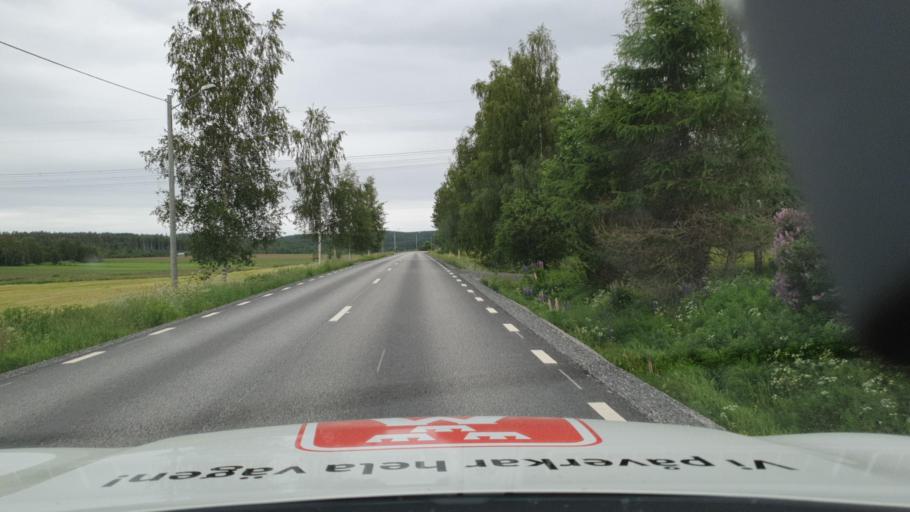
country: SE
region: Vaesterbotten
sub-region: Vannas Kommun
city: Vaennaes
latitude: 63.7448
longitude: 19.6483
